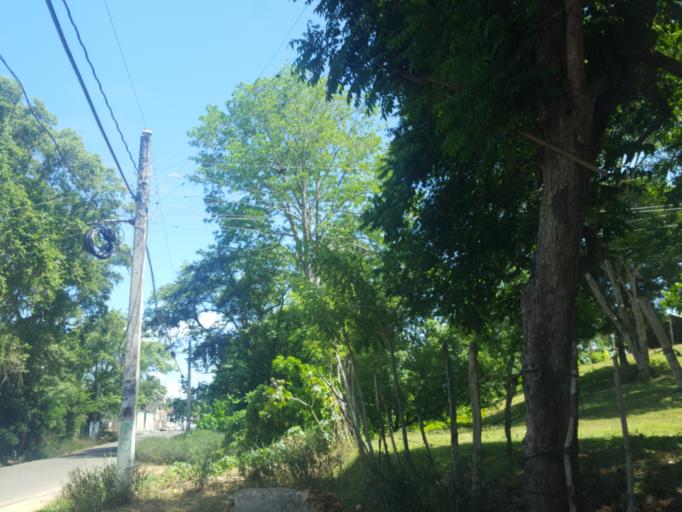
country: DO
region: Santiago
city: Baitoa
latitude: 19.3779
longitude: -70.6519
